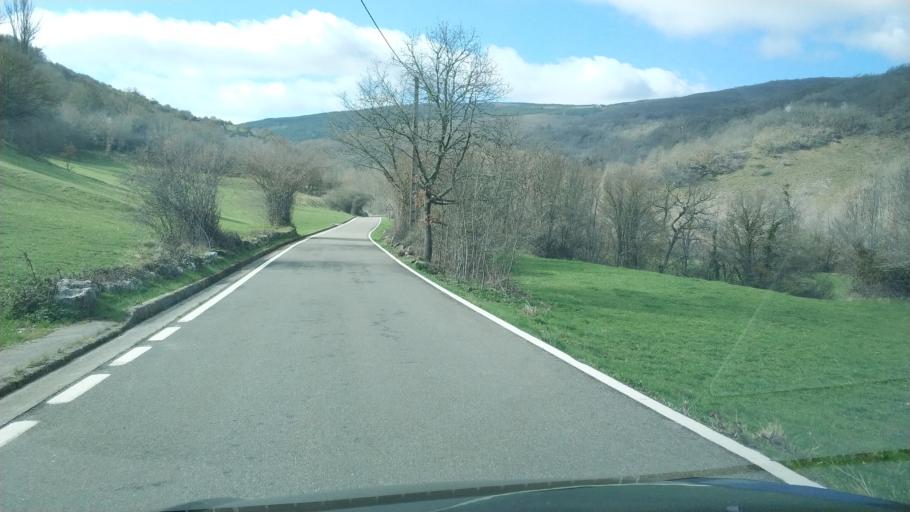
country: ES
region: Castille and Leon
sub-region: Provincia de Palencia
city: Berzosilla
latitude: 42.9041
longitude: -4.0320
